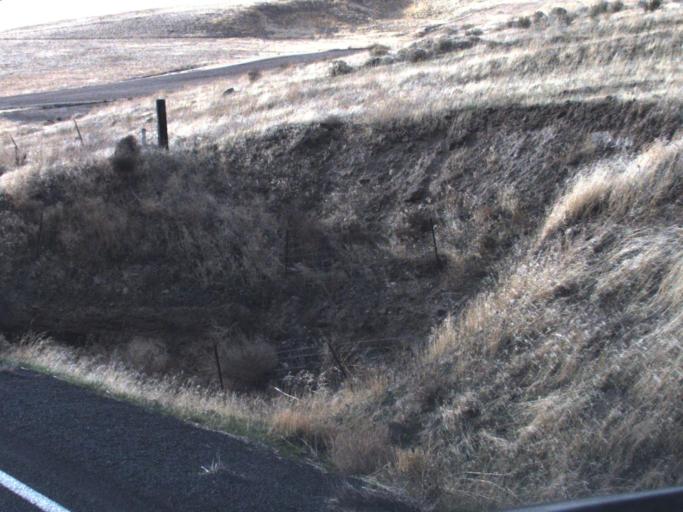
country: US
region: Washington
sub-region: Garfield County
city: Pomeroy
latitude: 46.4720
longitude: -117.6692
